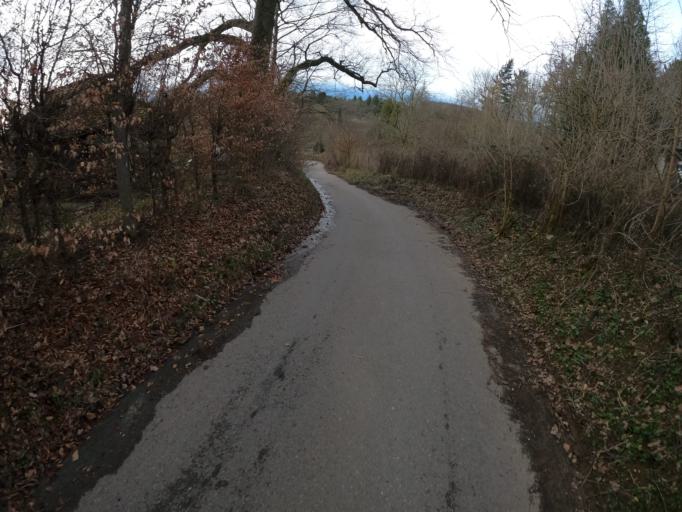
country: DE
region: Baden-Wuerttemberg
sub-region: Regierungsbezirk Stuttgart
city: Rechberghausen
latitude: 48.7162
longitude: 9.6328
